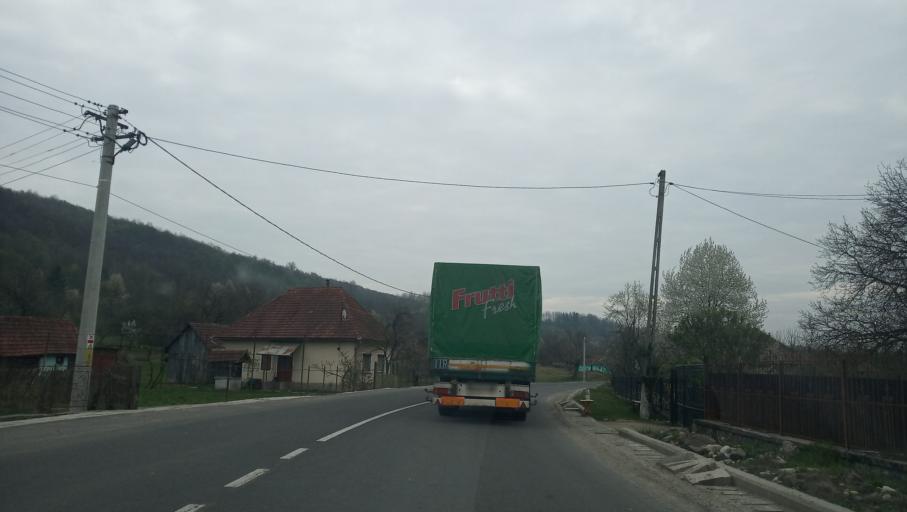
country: RO
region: Arad
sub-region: Comuna Varfurile
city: Varfurile
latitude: 46.3418
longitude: 22.5596
